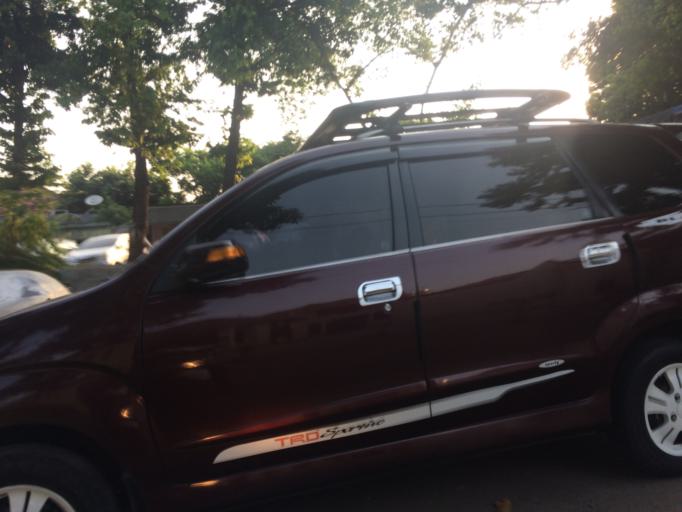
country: ID
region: Jakarta Raya
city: Jakarta
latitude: -6.2039
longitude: 106.8426
